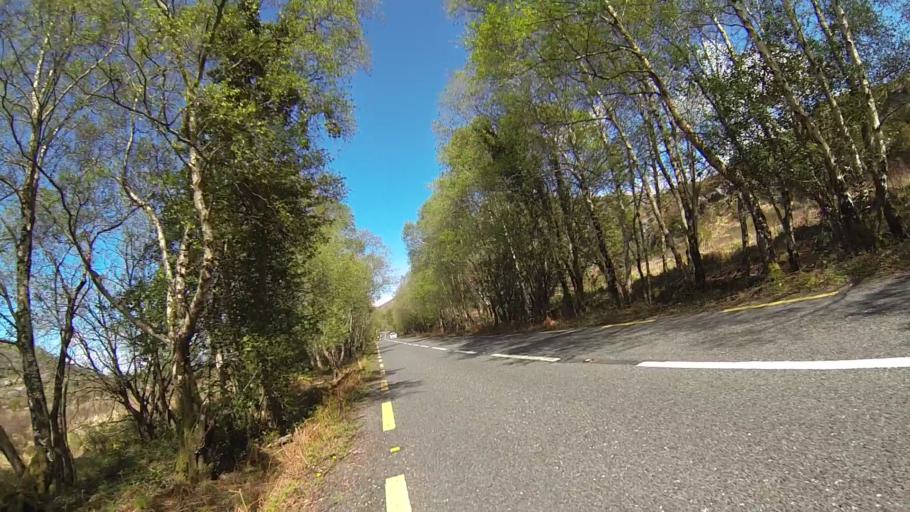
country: IE
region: Munster
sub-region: Ciarrai
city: Cill Airne
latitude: 51.9891
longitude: -9.5563
